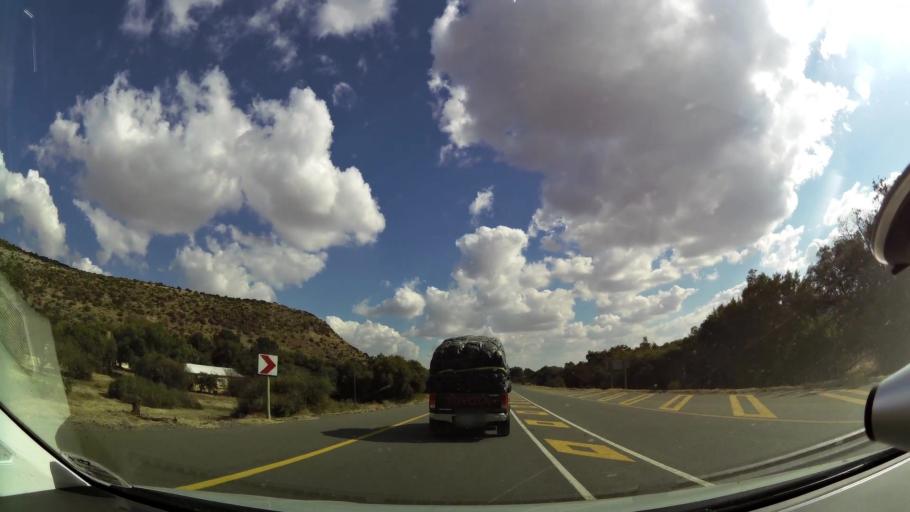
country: ZA
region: Orange Free State
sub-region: Mangaung Metropolitan Municipality
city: Bloemfontein
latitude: -29.1590
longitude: 26.0519
